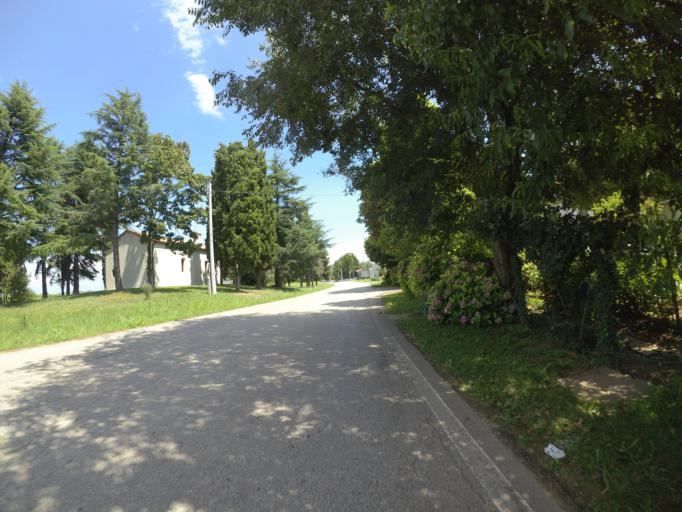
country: IT
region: Friuli Venezia Giulia
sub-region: Provincia di Udine
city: Lestizza
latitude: 45.9617
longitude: 13.1056
